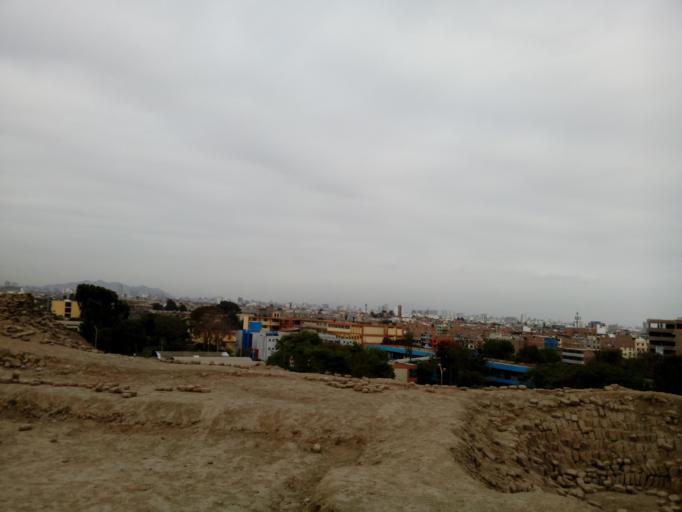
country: PE
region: Callao
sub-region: Callao
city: Callao
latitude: -12.0600
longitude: -77.0861
